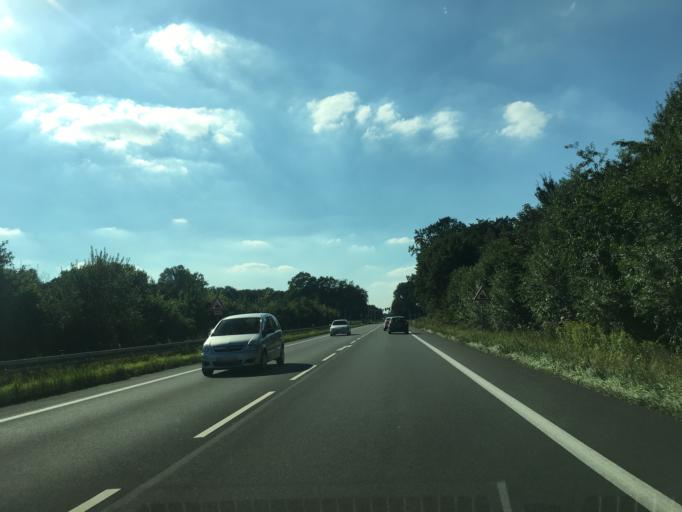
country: DE
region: North Rhine-Westphalia
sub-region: Regierungsbezirk Munster
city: Sassenberg
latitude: 51.9463
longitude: 8.0381
